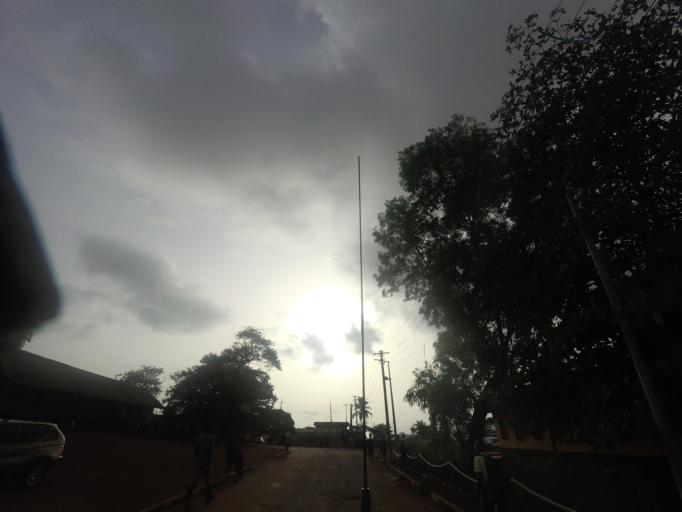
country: SL
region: Western Area
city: Freetown
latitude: 8.4904
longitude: -13.2660
